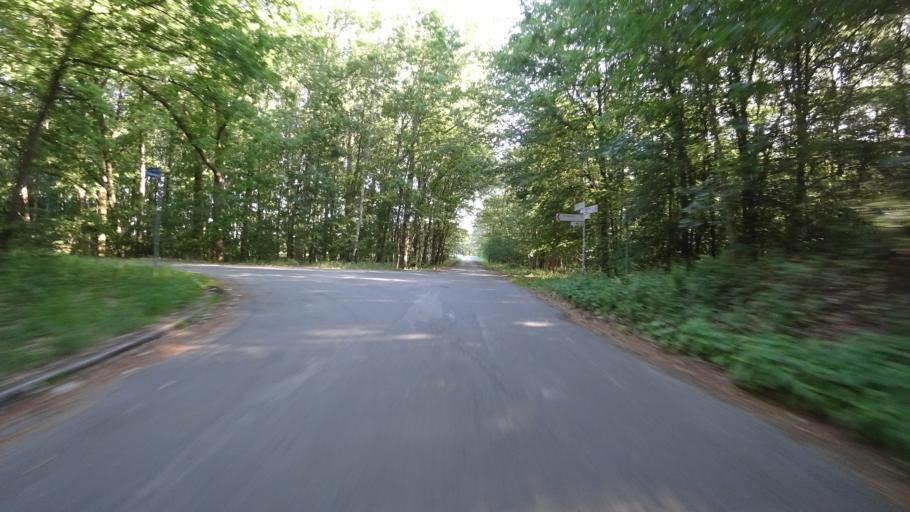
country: DE
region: North Rhine-Westphalia
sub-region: Regierungsbezirk Detmold
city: Rheda-Wiedenbruck
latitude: 51.8794
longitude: 8.3159
